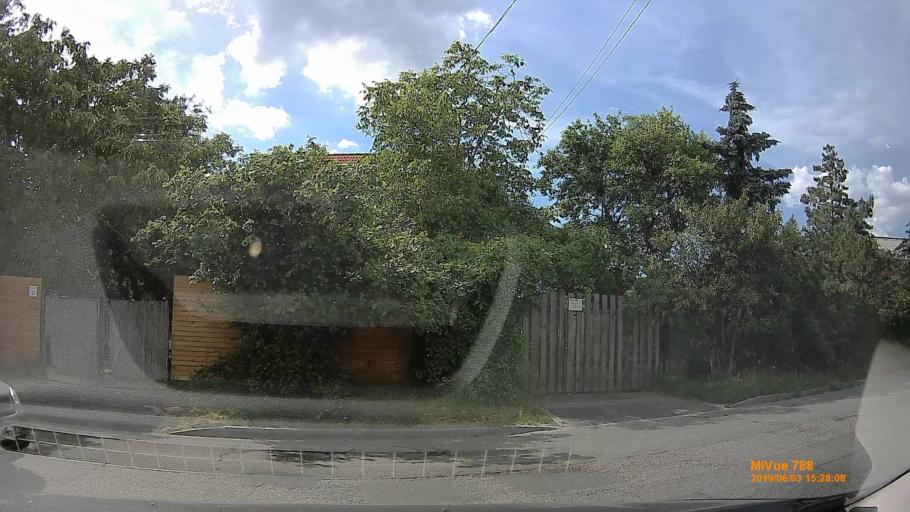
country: HU
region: Budapest
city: Budapest XXII. keruelet
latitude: 47.4348
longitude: 19.0130
